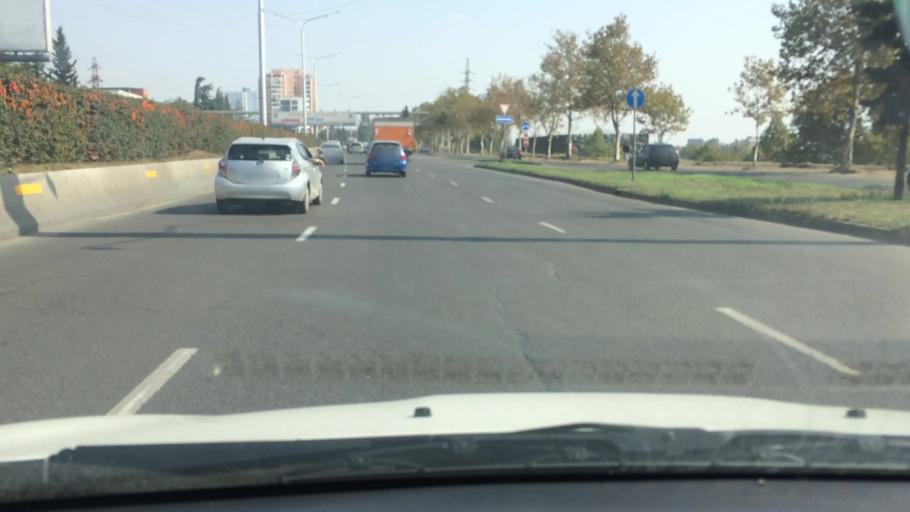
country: GE
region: T'bilisi
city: Tbilisi
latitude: 41.6880
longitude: 44.8468
